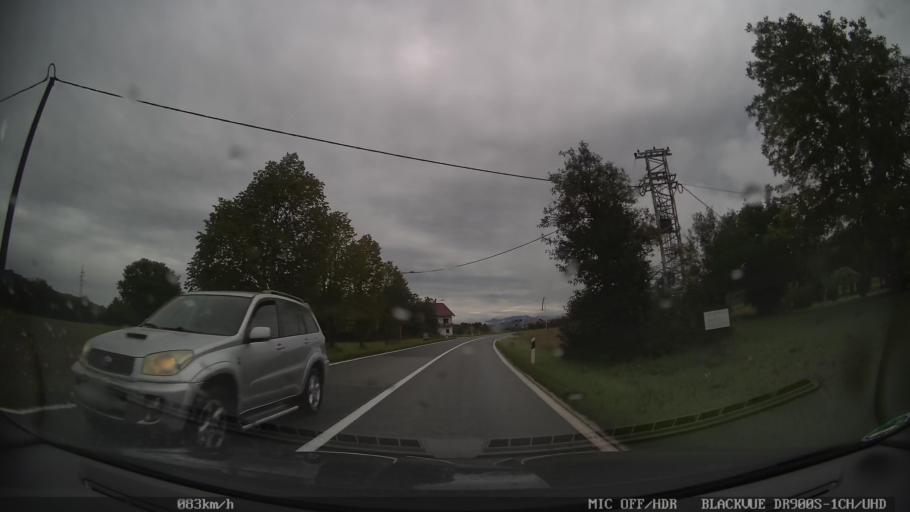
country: HR
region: Licko-Senjska
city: Brinje
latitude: 44.9487
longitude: 15.1254
